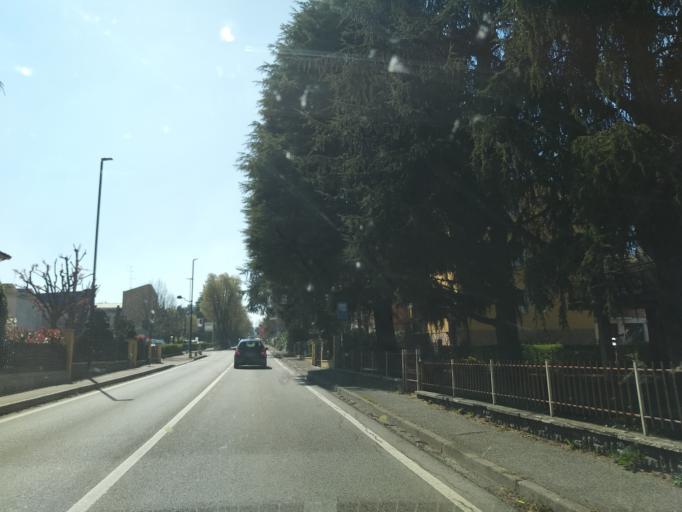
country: IT
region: Emilia-Romagna
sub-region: Provincia di Reggio Emilia
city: Albinea
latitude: 44.6240
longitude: 10.6052
